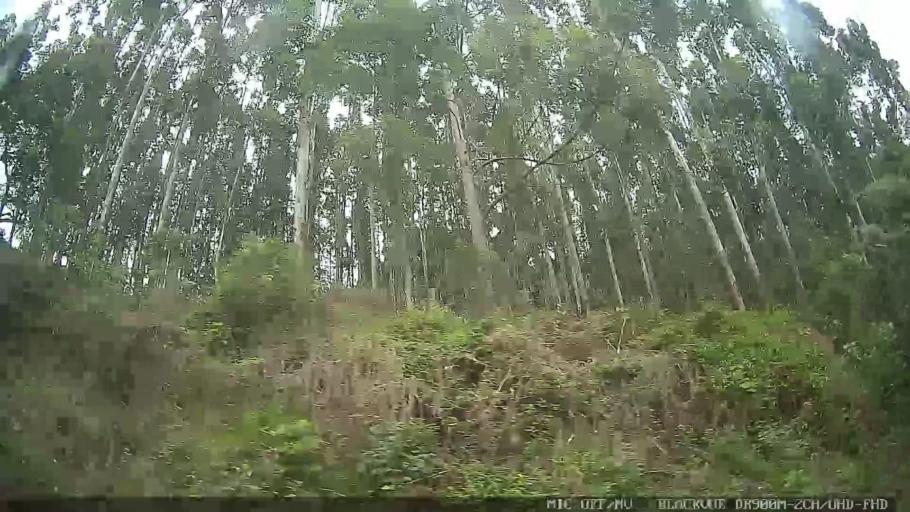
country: BR
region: Sao Paulo
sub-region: Serra Negra
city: Serra Negra
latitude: -22.6144
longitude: -46.7432
